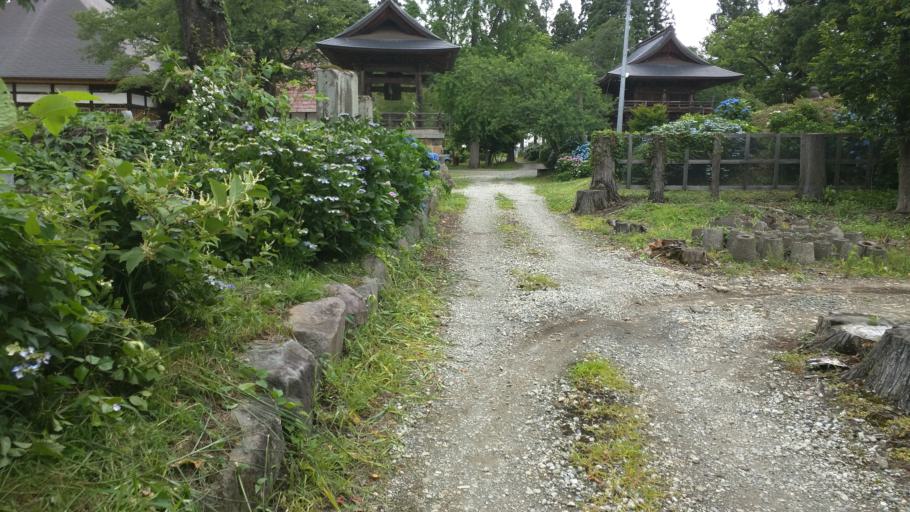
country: JP
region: Fukushima
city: Kitakata
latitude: 37.6874
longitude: 139.8633
